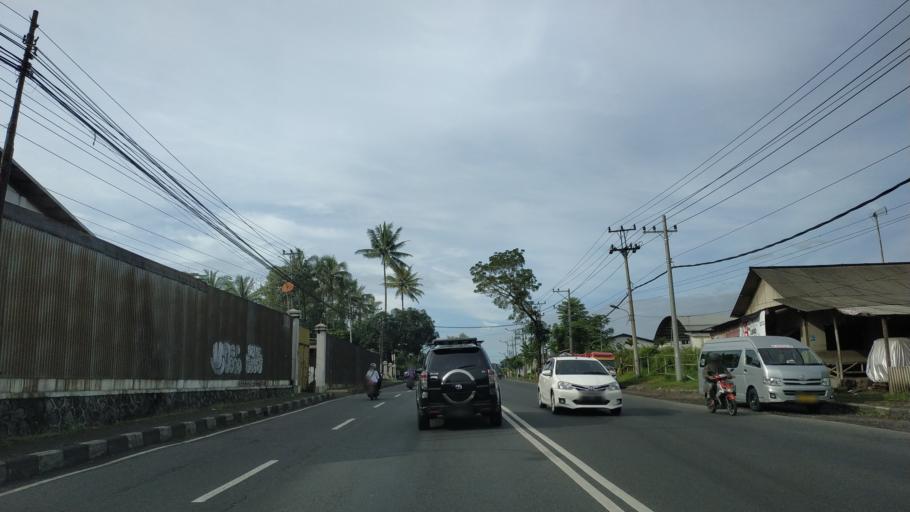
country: ID
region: Central Java
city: Salatiga
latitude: -7.3727
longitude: 110.5150
